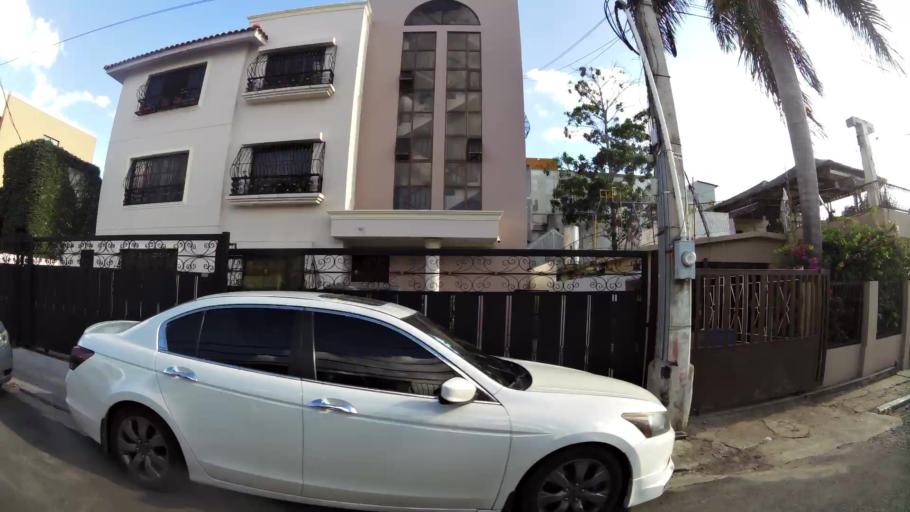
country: DO
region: Santiago
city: Santiago de los Caballeros
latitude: 19.4615
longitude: -70.6914
